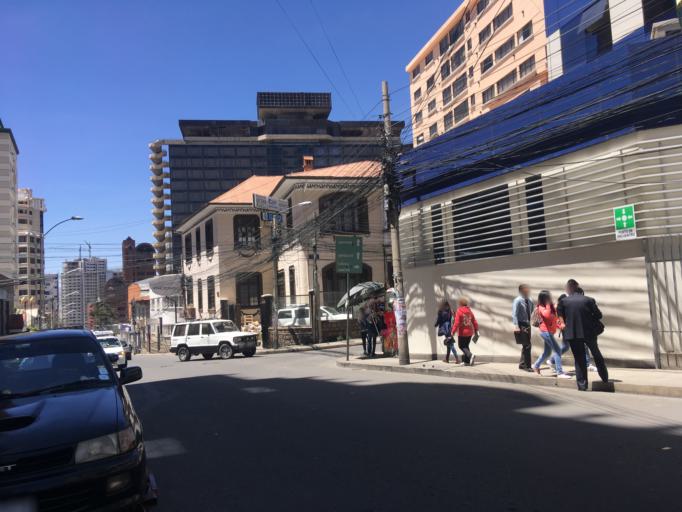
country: BO
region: La Paz
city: La Paz
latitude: -16.5054
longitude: -68.1280
